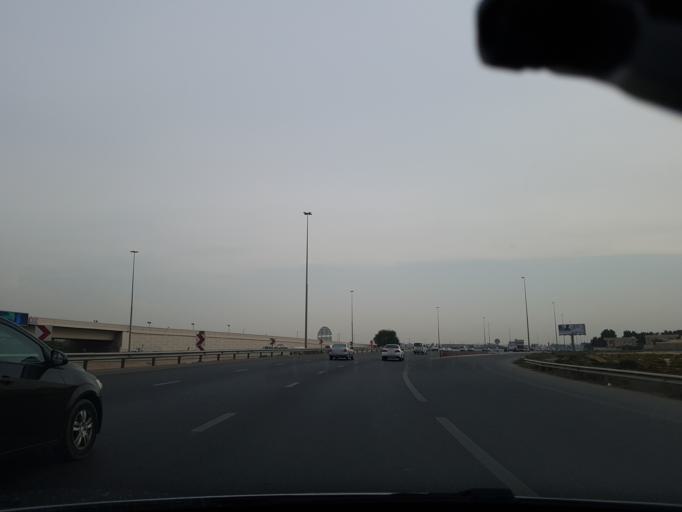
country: AE
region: Ajman
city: Ajman
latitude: 25.3575
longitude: 55.4808
